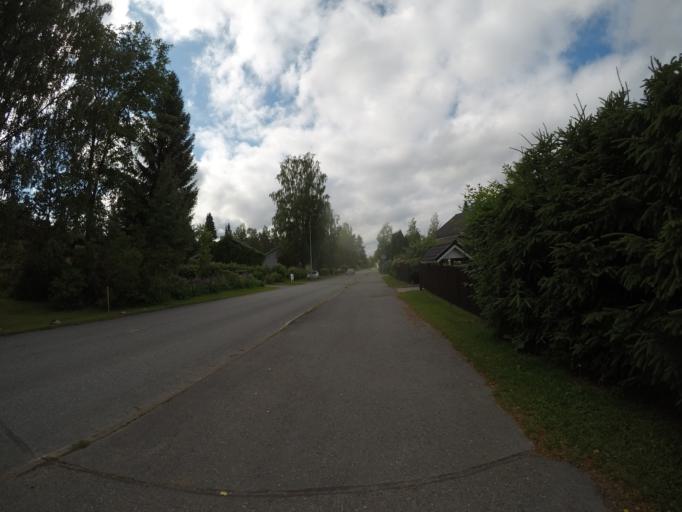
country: FI
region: Haeme
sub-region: Haemeenlinna
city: Haemeenlinna
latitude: 60.9837
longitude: 24.4422
